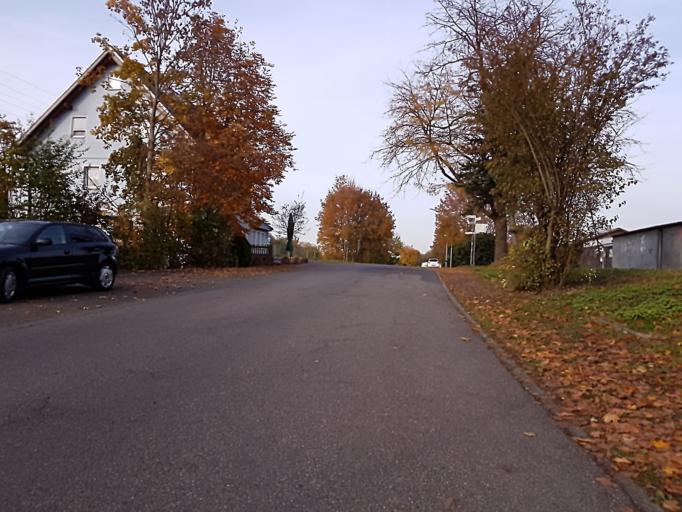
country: DE
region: Bavaria
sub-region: Regierungsbezirk Unterfranken
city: Elsenfeld
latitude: 49.8402
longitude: 9.1533
